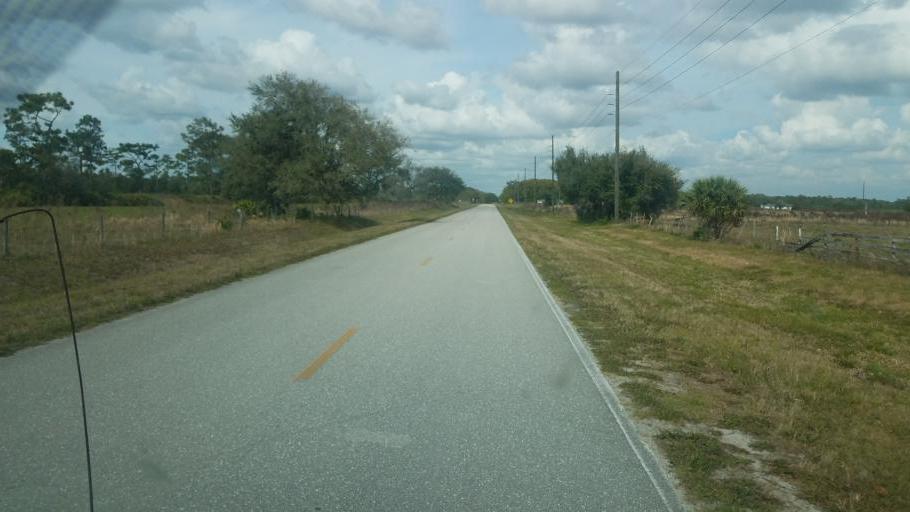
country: US
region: Florida
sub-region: Okeechobee County
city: Cypress Quarters
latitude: 27.5127
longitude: -80.7766
